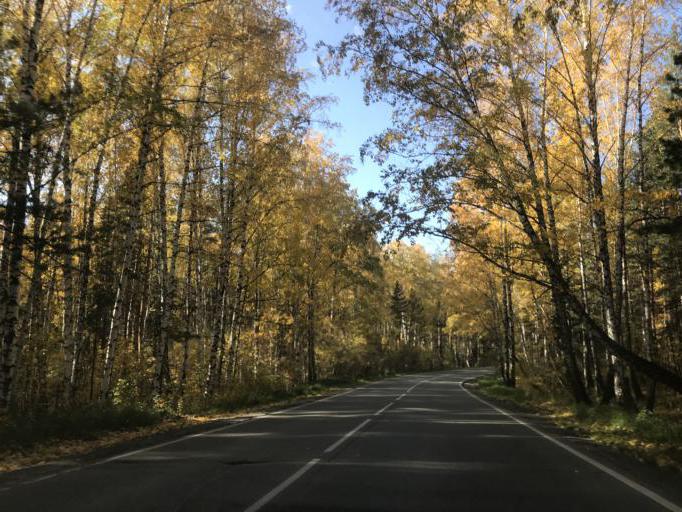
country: RU
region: Chelyabinsk
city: Dolgoderevenskoye
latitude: 55.2835
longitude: 61.3608
